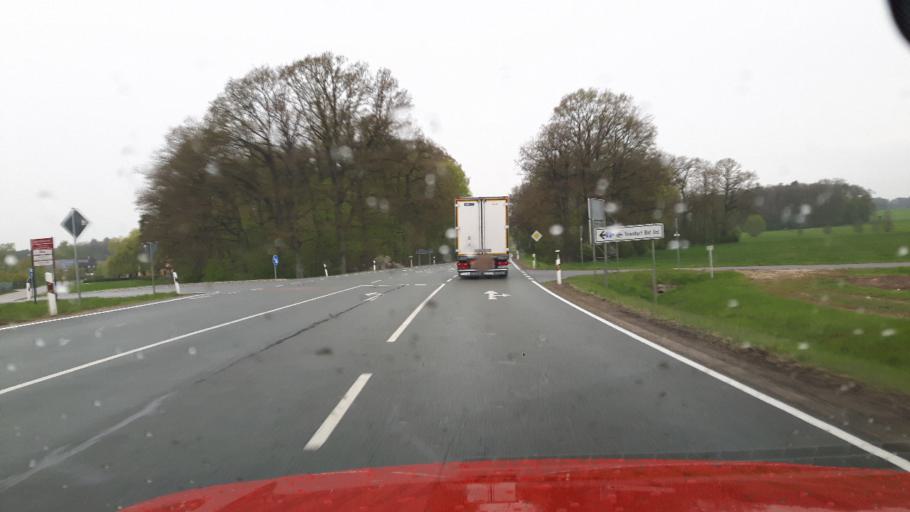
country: DE
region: Bavaria
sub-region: Regierungsbezirk Mittelfranken
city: Merkendorf
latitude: 49.2012
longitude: 10.6848
